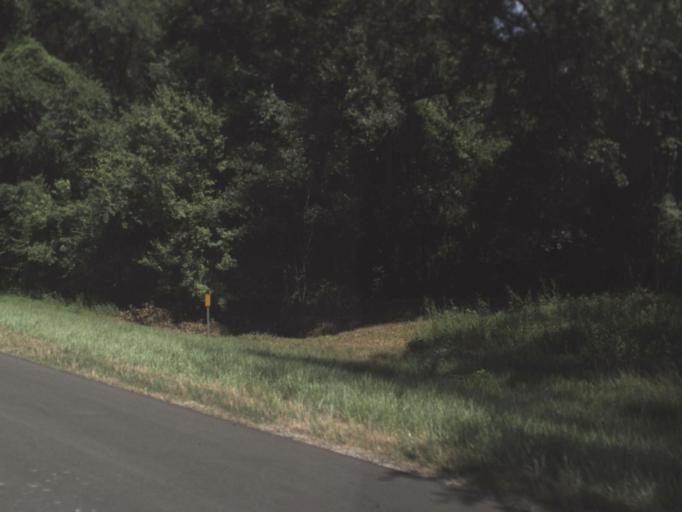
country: US
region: Florida
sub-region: Madison County
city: Madison
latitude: 30.4101
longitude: -83.4170
